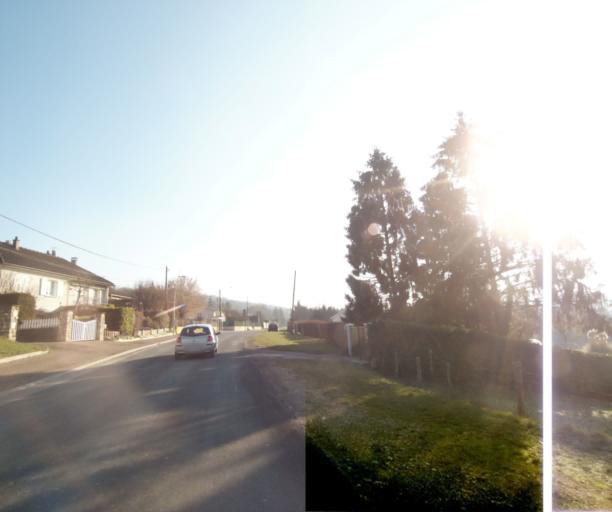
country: FR
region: Champagne-Ardenne
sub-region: Departement de la Haute-Marne
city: Chevillon
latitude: 48.5214
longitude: 5.1170
